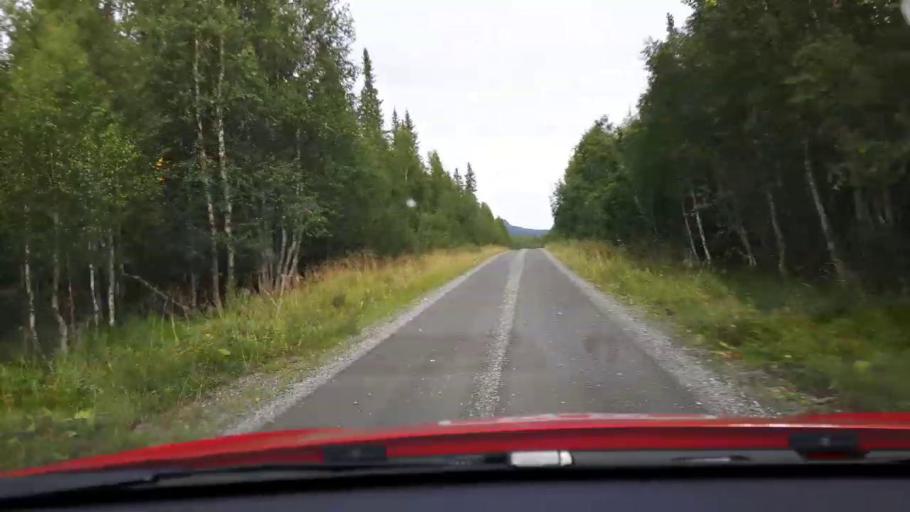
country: SE
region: Jaemtland
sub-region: Are Kommun
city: Are
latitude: 63.7776
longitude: 13.0981
